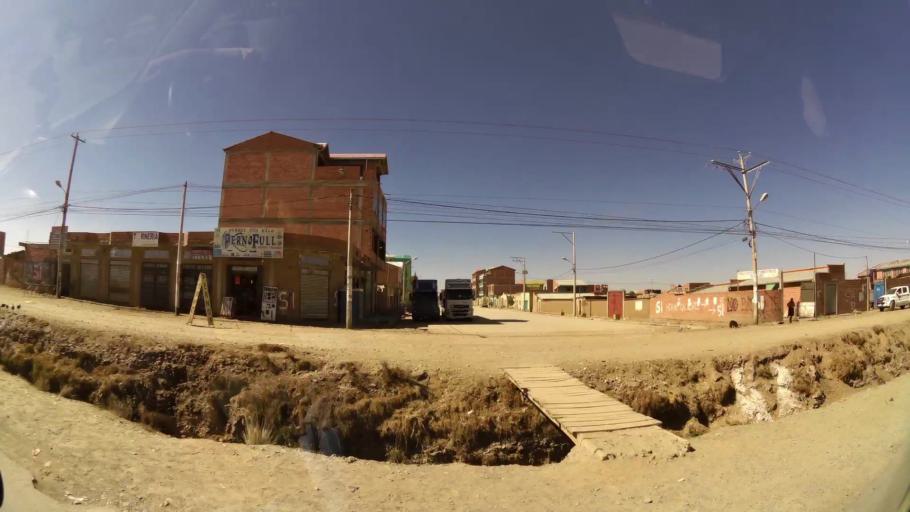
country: BO
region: La Paz
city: La Paz
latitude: -16.5572
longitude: -68.2112
